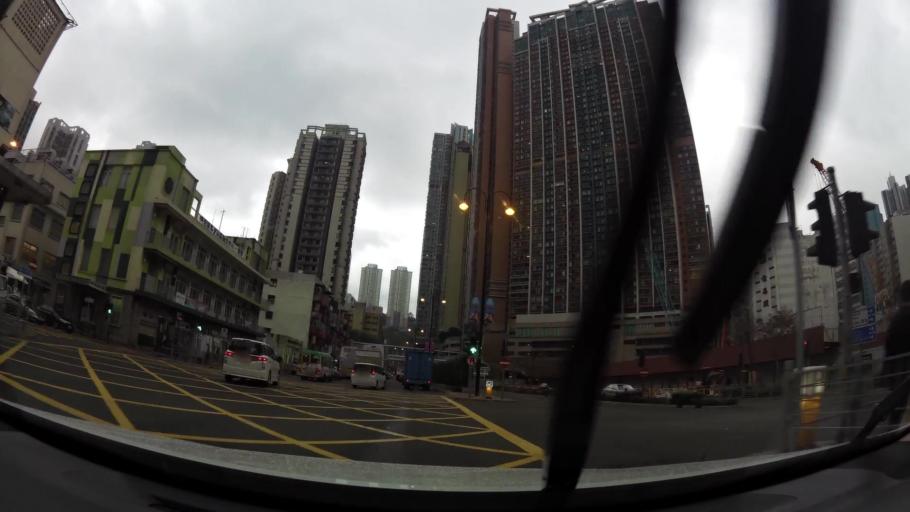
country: HK
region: Tsuen Wan
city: Tsuen Wan
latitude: 22.3682
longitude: 114.1155
